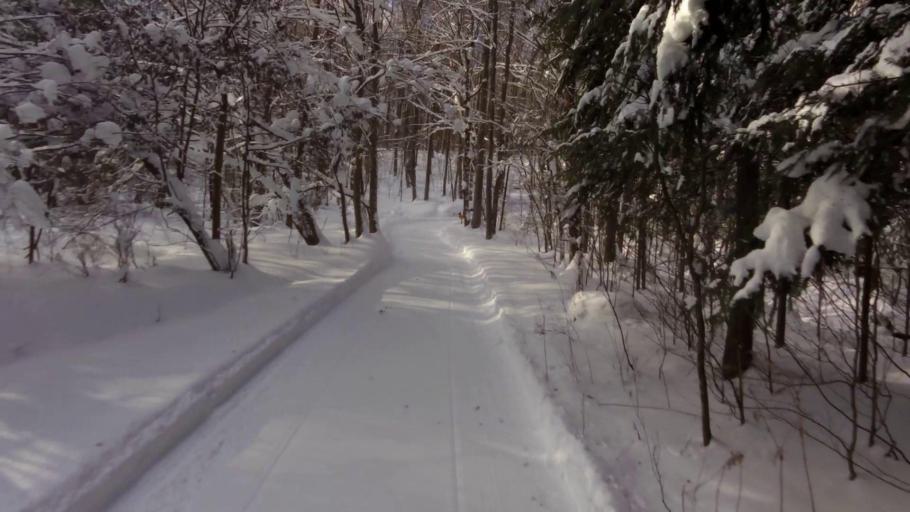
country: US
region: New York
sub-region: Chautauqua County
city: Falconer
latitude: 42.2499
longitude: -79.1508
